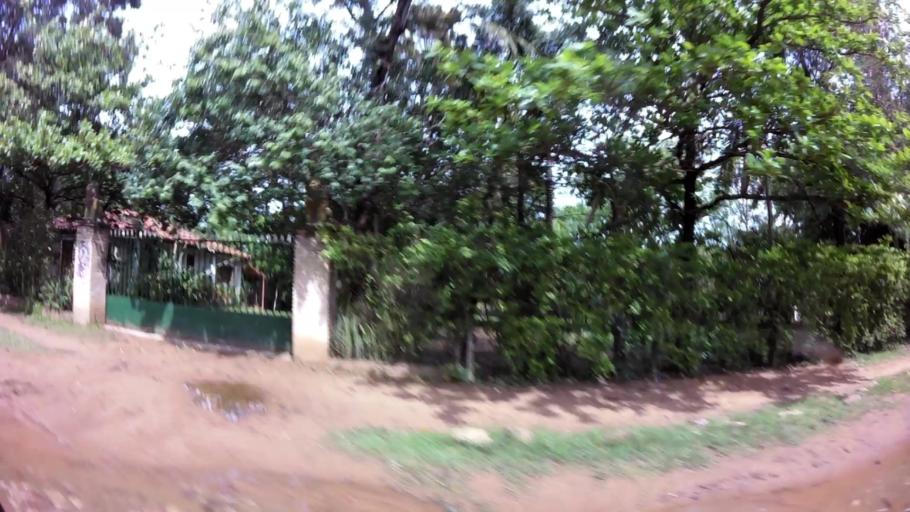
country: PY
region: Central
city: Limpio
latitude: -25.1844
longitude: -57.4774
